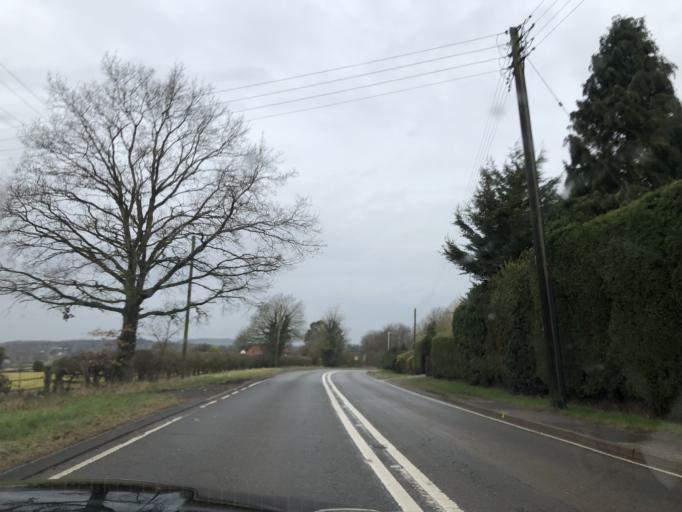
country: GB
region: England
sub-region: Warwickshire
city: Henley in Arden
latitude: 52.2856
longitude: -1.7596
